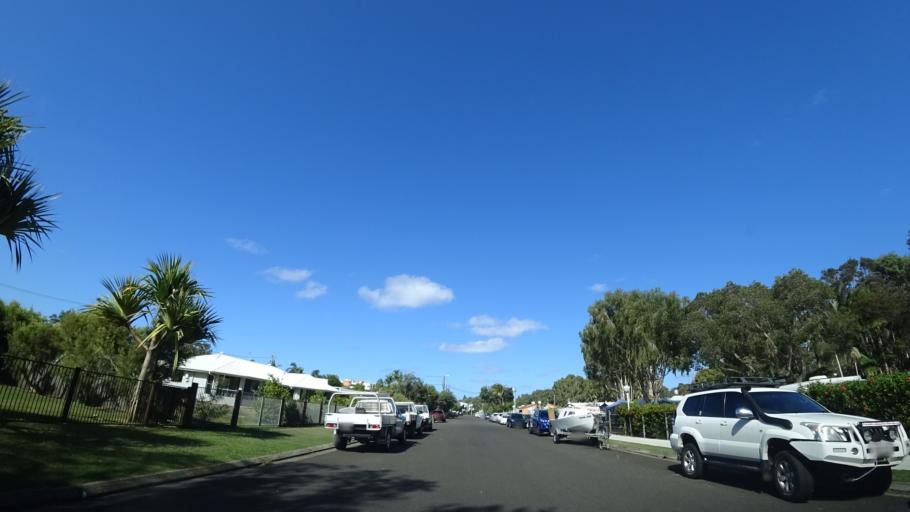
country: AU
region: Queensland
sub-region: Sunshine Coast
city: Mooloolaba
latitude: -26.6176
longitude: 153.0980
